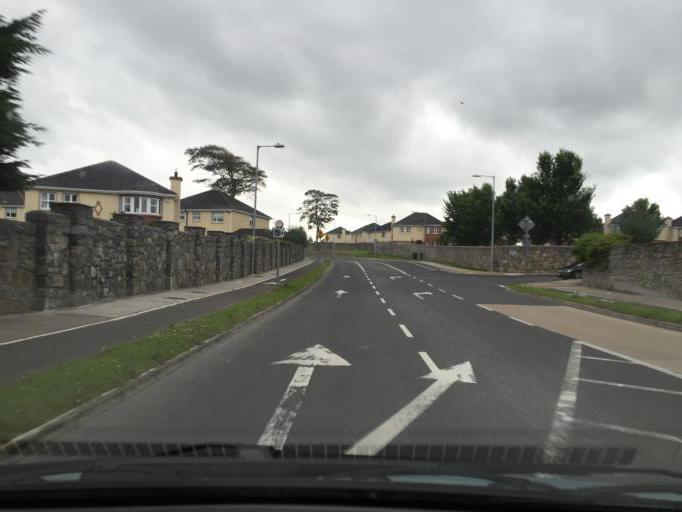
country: IE
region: Connaught
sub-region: Sligo
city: Sligo
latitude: 54.2715
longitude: -8.5032
